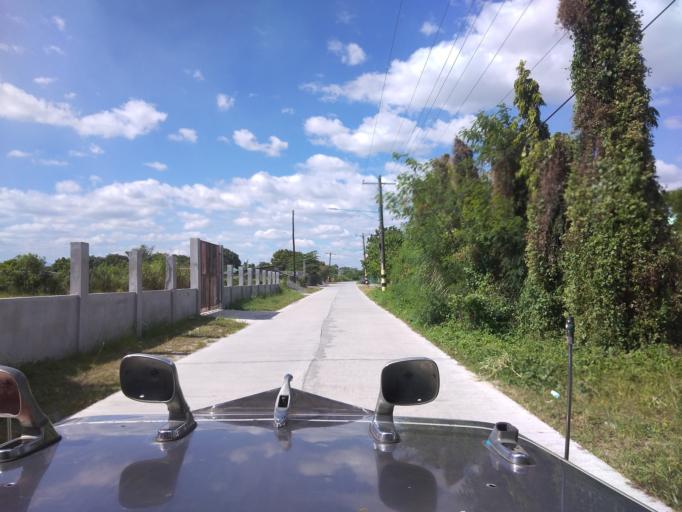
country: PH
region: Central Luzon
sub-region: Province of Pampanga
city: Bacolor
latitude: 15.0234
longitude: 120.6377
